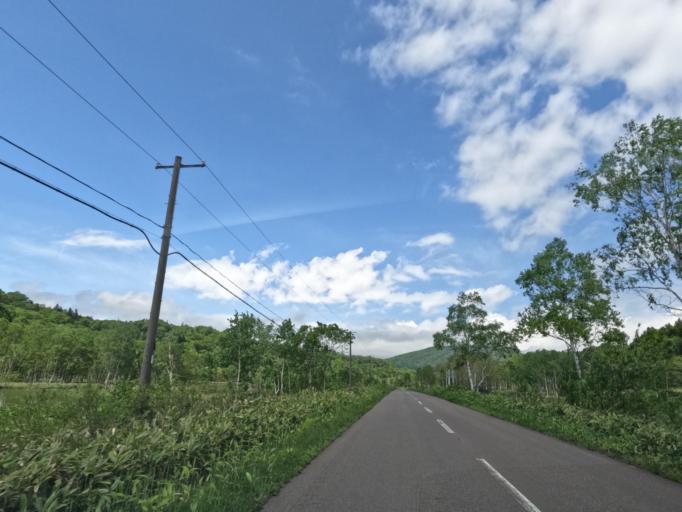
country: JP
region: Hokkaido
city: Tobetsu
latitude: 43.5212
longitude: 141.5873
